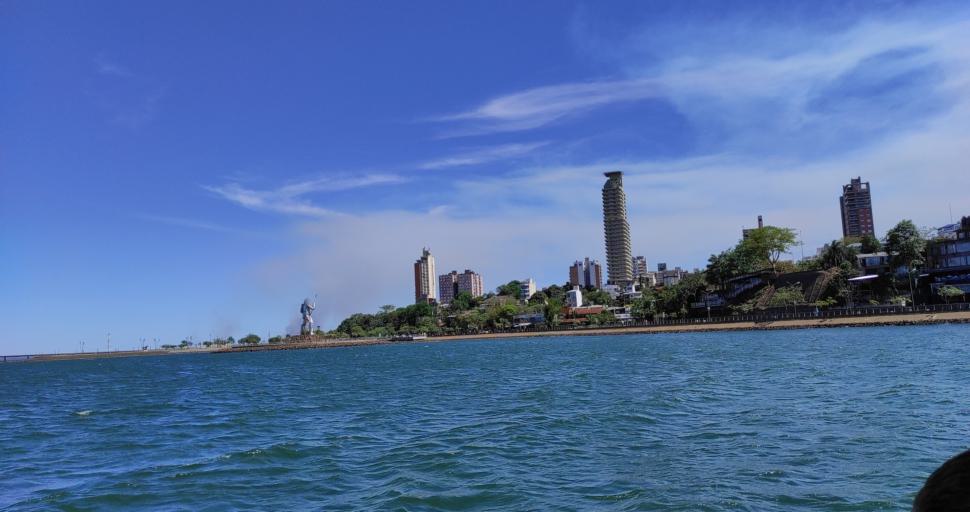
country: AR
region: Misiones
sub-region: Departamento de Capital
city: Posadas
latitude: -27.3577
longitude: -55.8888
